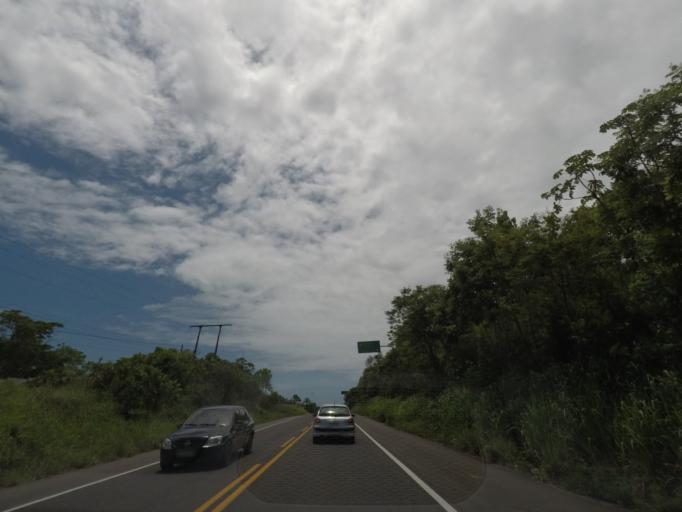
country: BR
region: Bahia
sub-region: Itaparica
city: Itaparica
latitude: -12.9479
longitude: -38.6320
